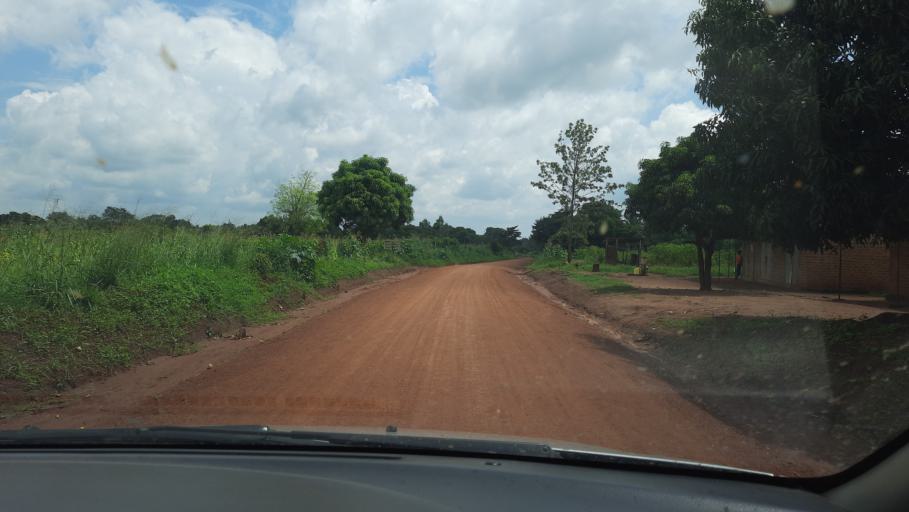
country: UG
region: Western Region
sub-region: Kiryandongo District
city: Kiryandongo
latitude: 1.8165
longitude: 31.9911
